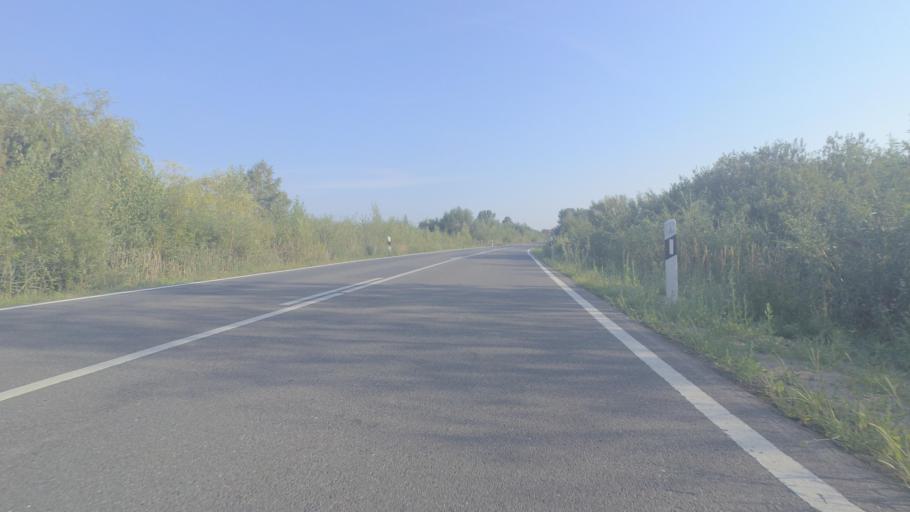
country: DE
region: Mecklenburg-Vorpommern
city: Demmin
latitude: 53.9641
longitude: 13.1322
